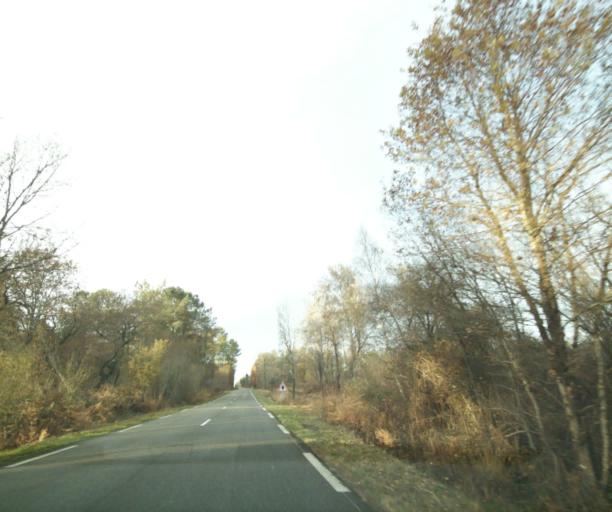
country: FR
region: Aquitaine
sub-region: Departement des Landes
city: Gabarret
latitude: 44.0325
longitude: -0.0304
